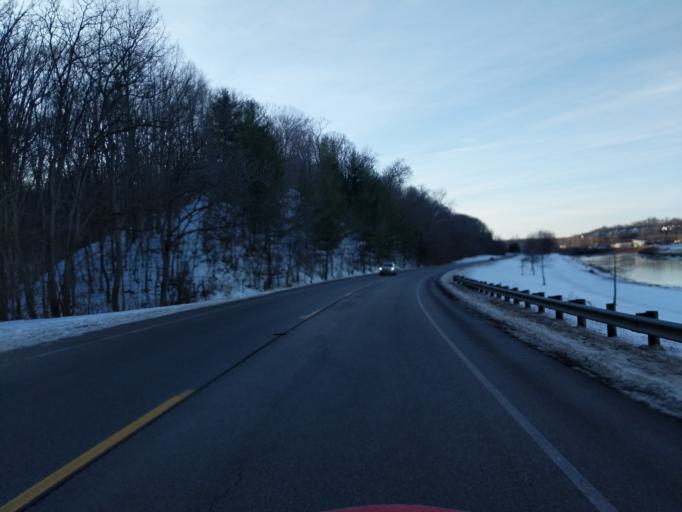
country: US
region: Ohio
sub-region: Athens County
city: Athens
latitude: 39.3255
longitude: -82.1168
